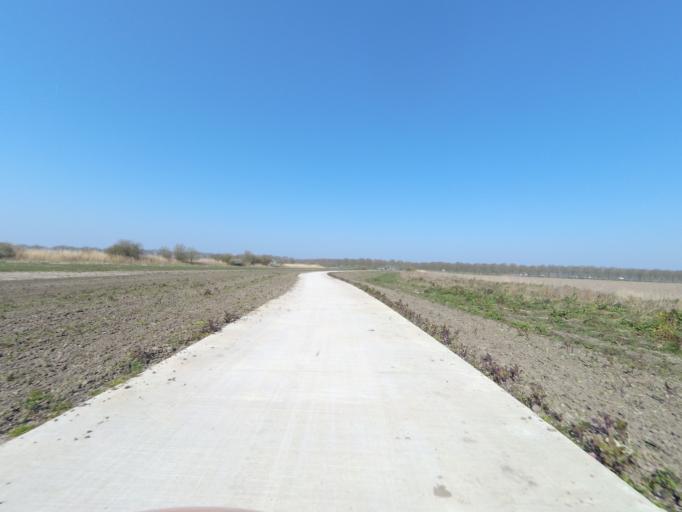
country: NL
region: Flevoland
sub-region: Gemeente Almere
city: Almere Stad
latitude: 52.3908
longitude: 5.3536
